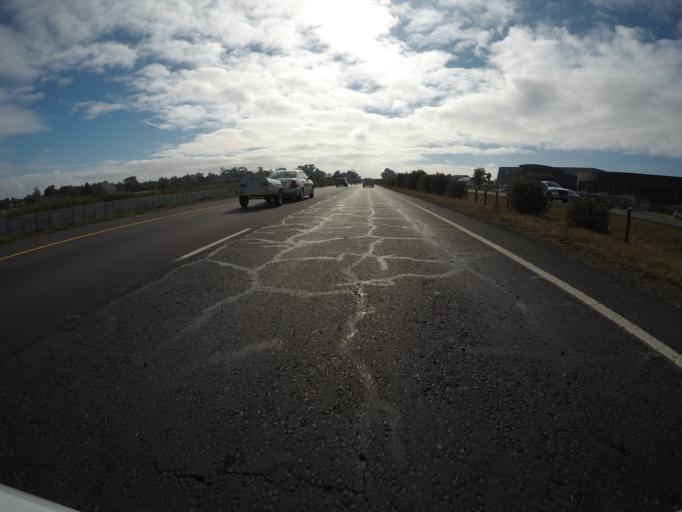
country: ZA
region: Western Cape
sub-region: City of Cape Town
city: Kraaifontein
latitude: -33.8372
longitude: 18.7291
